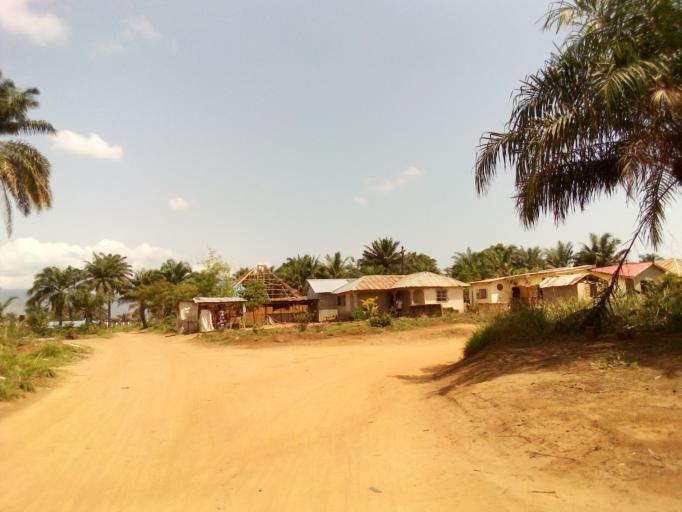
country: SL
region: Western Area
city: Waterloo
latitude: 8.3493
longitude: -13.0181
